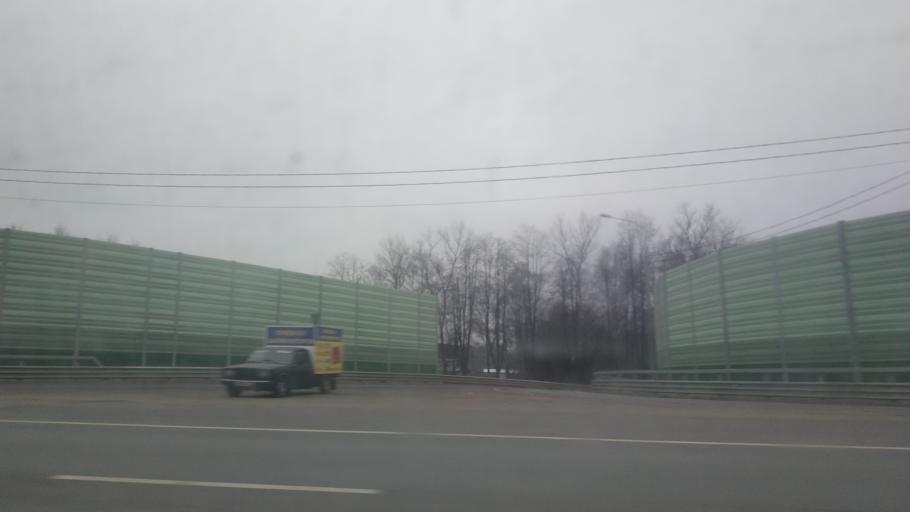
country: RU
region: Moscow
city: Severnyy
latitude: 55.9593
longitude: 37.5330
